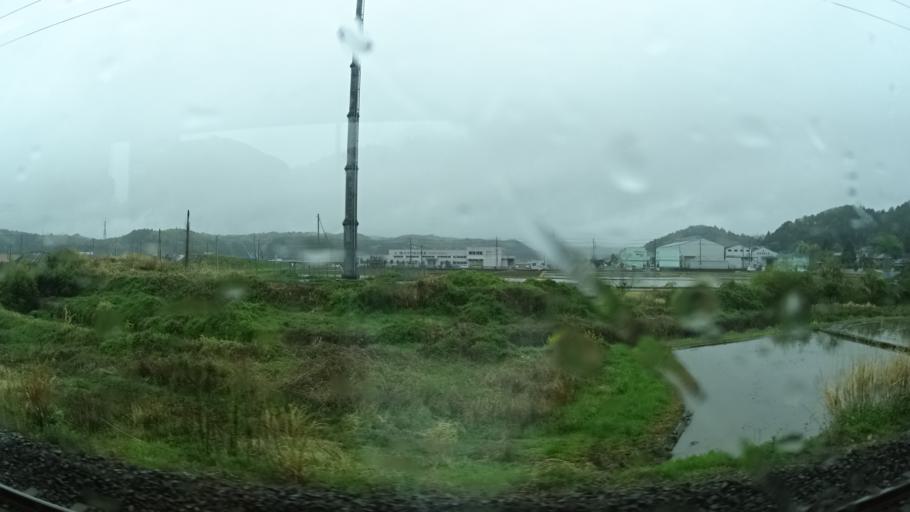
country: JP
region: Ibaraki
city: Kitaibaraki
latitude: 36.8514
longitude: 140.7788
